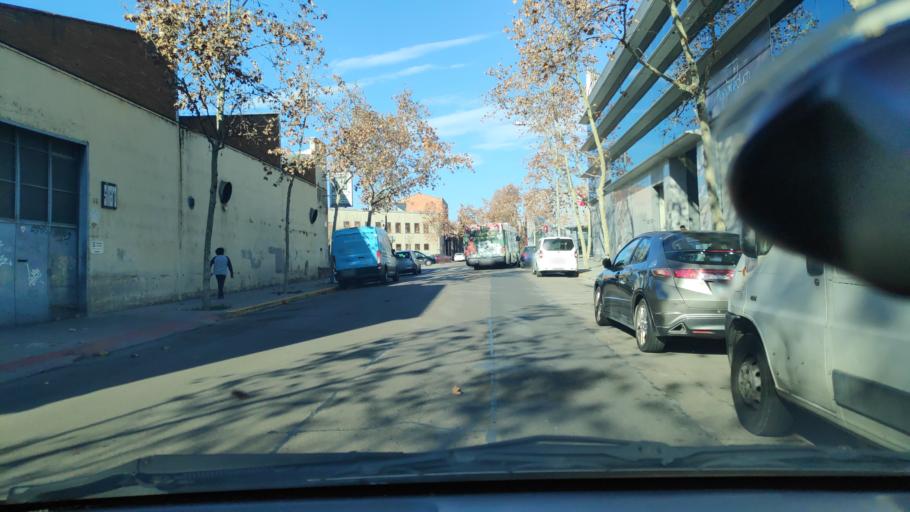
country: ES
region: Catalonia
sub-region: Provincia de Barcelona
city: Sabadell
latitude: 41.5349
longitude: 2.0990
